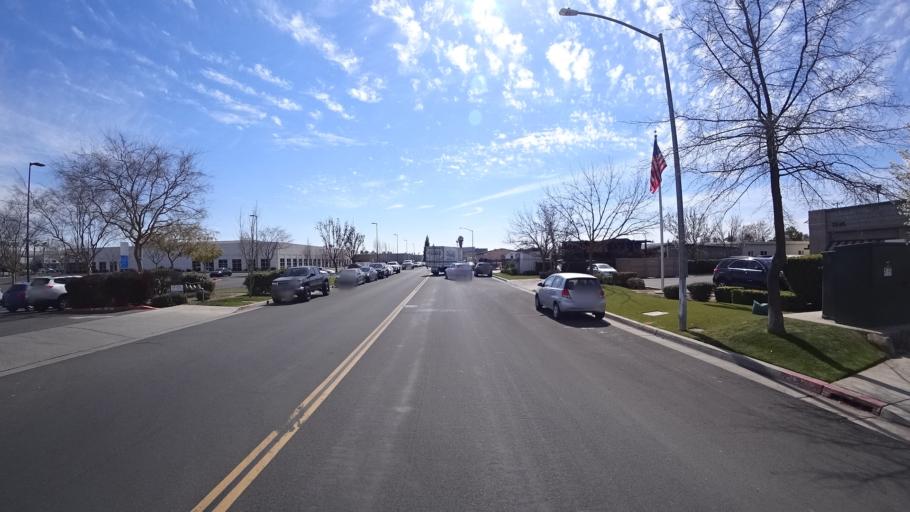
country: US
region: California
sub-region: Fresno County
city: Fresno
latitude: 36.8426
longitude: -119.8098
